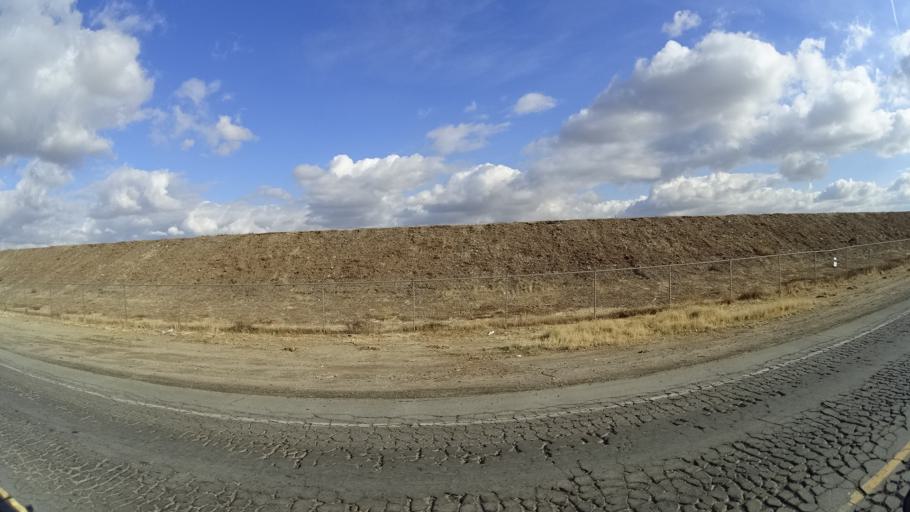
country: US
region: California
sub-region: Kern County
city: Bakersfield
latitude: 35.3365
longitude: -118.9677
